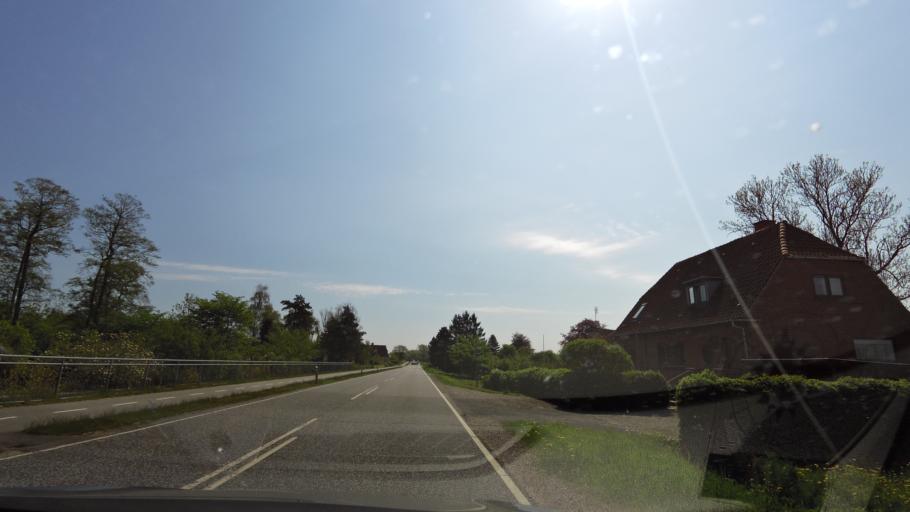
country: DK
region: South Denmark
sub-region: Nyborg Kommune
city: Nyborg
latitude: 55.2414
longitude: 10.7127
